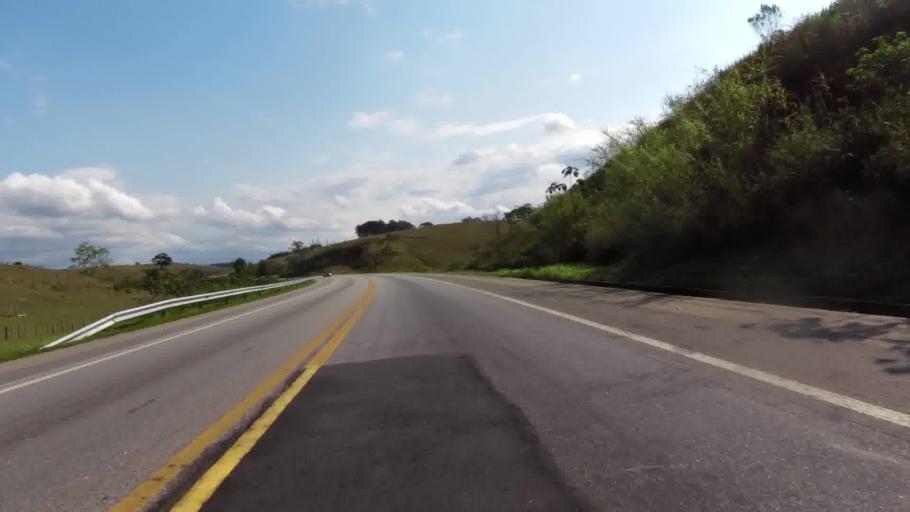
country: BR
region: Rio de Janeiro
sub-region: Macae
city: Macae
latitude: -22.2533
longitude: -41.8289
